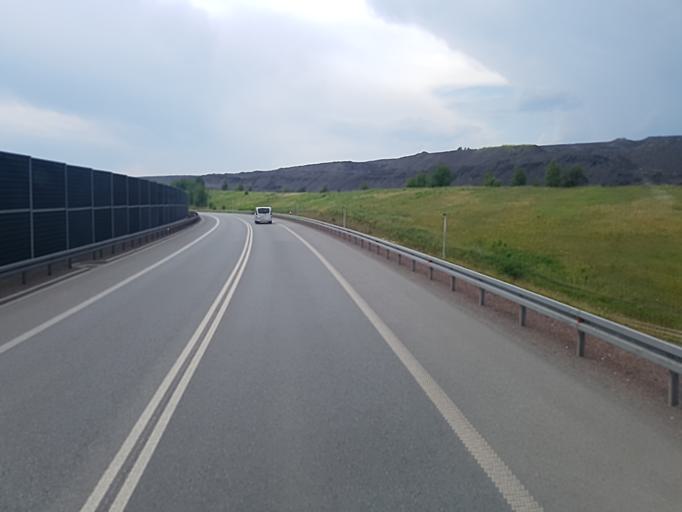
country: PL
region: Silesian Voivodeship
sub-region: Jastrzebie-Zdroj
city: Jastrzebie Zdroj
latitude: 49.9738
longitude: 18.5925
